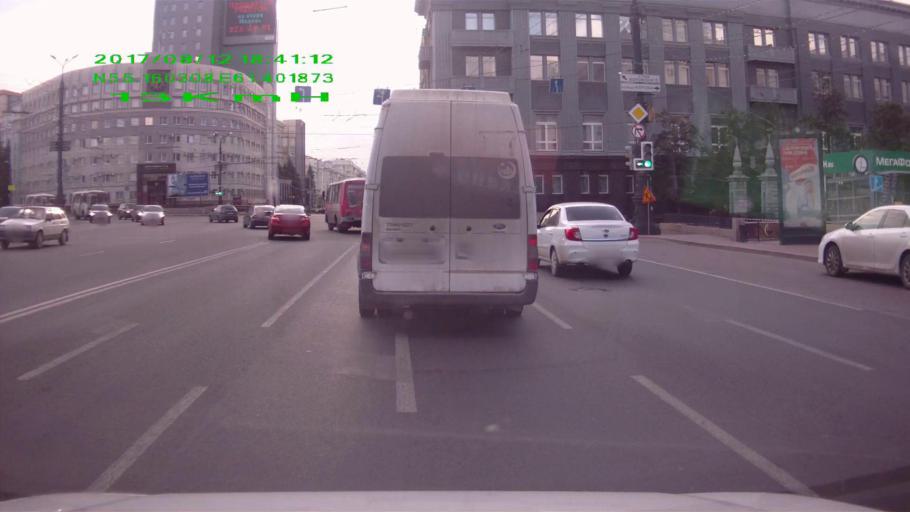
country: RU
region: Chelyabinsk
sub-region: Gorod Chelyabinsk
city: Chelyabinsk
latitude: 55.1579
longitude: 61.3979
